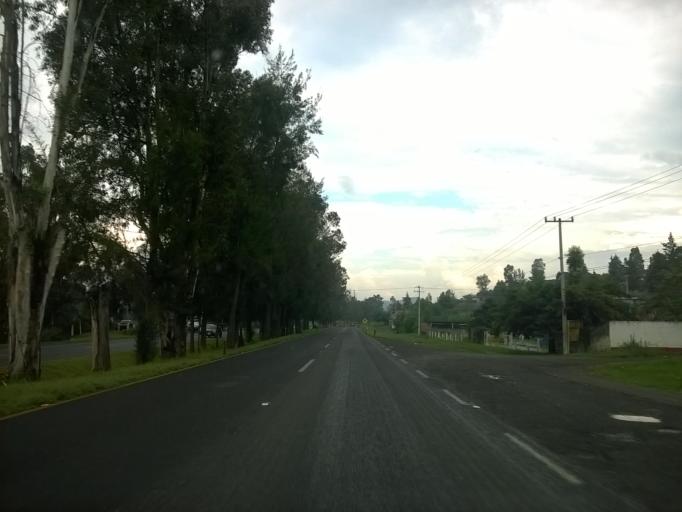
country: MX
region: Michoacan
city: Cuanajo
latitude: 19.5376
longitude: -101.5299
